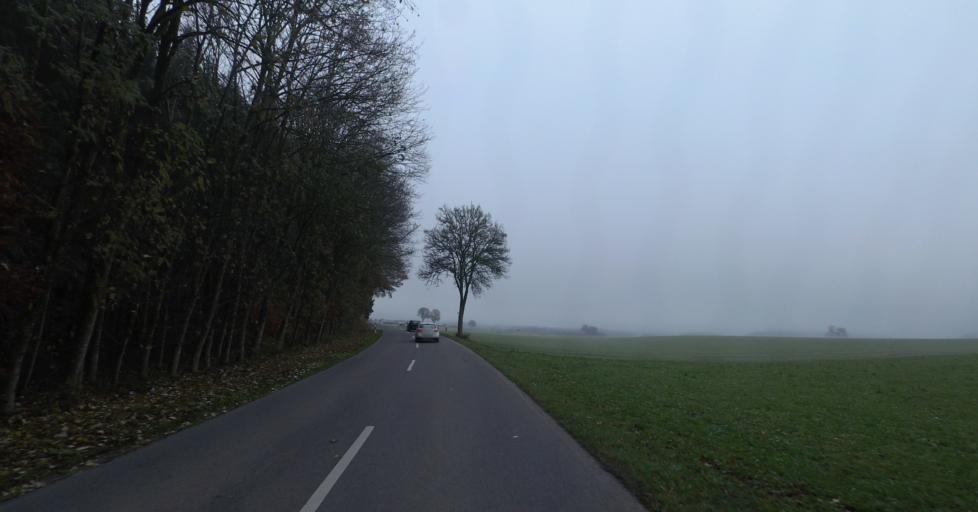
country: DE
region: Bavaria
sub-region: Upper Bavaria
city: Seeon-Seebruck
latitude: 47.9715
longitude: 12.5232
